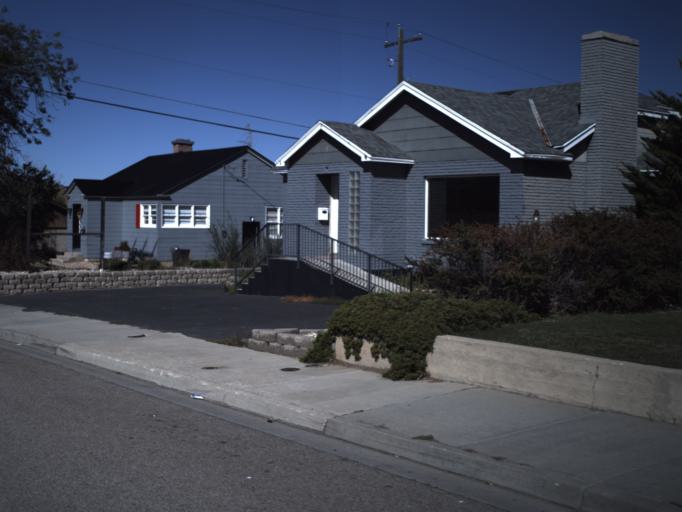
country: US
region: Utah
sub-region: Iron County
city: Cedar City
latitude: 37.6809
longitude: -113.0692
